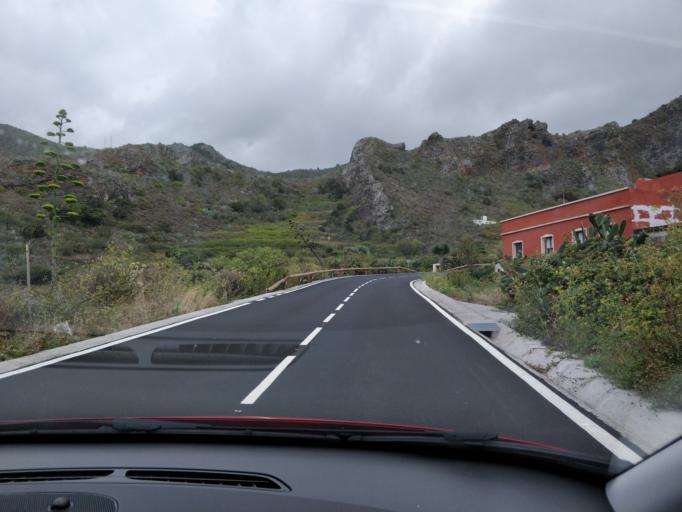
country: ES
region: Canary Islands
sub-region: Provincia de Santa Cruz de Tenerife
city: Tanque
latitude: 28.3483
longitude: -16.8442
